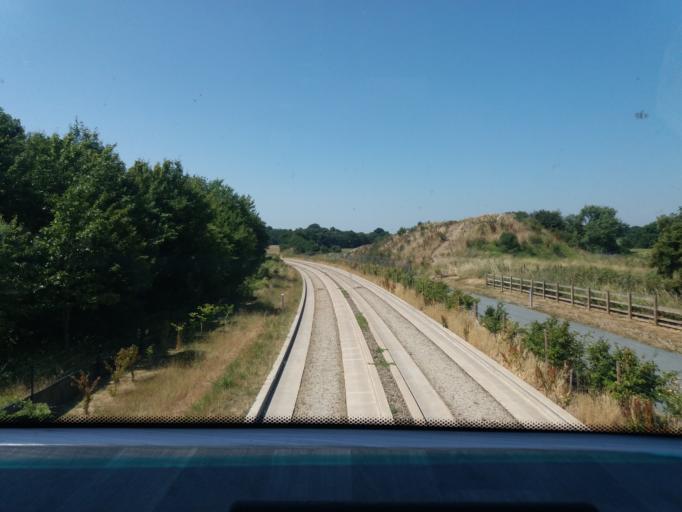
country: GB
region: England
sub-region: Borough of Wigan
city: Atherton
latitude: 53.5101
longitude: -2.4847
